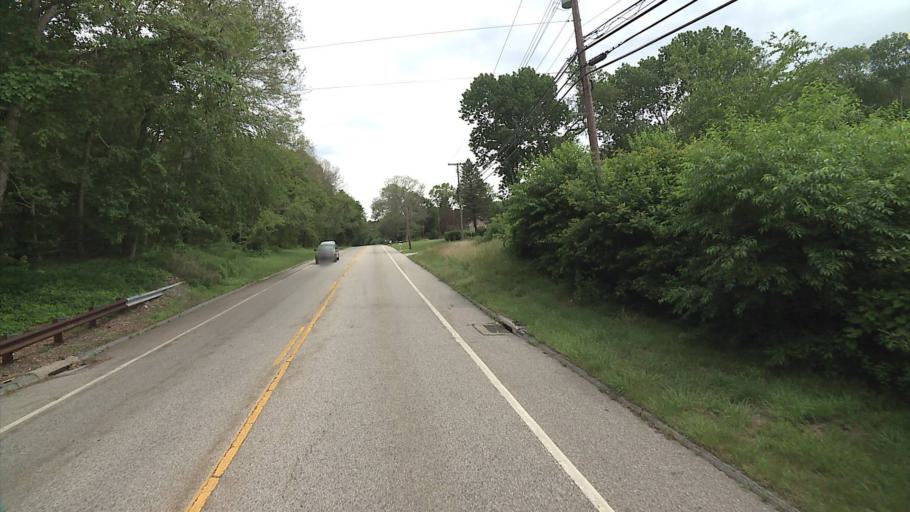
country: US
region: Connecticut
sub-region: New London County
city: Poquonock Bridge
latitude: 41.3775
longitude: -72.0266
